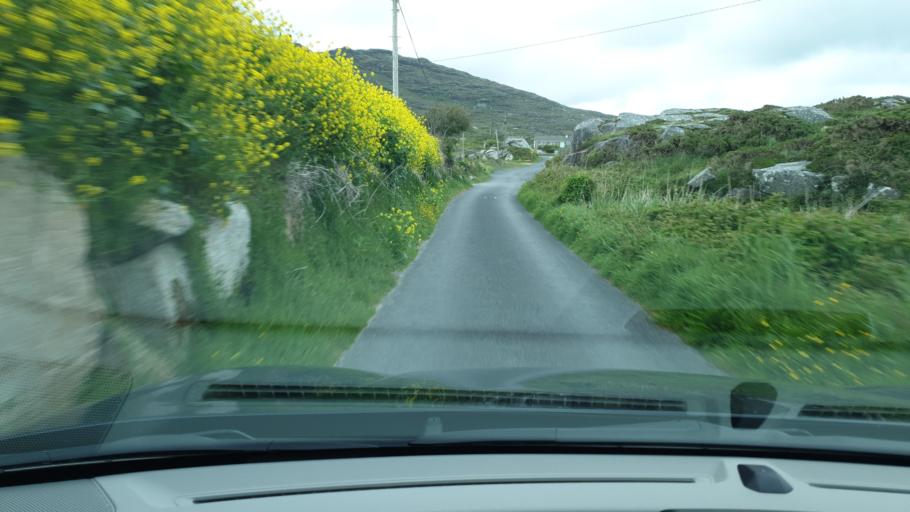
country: IE
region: Connaught
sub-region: County Galway
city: Clifden
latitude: 53.3823
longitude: -9.9523
